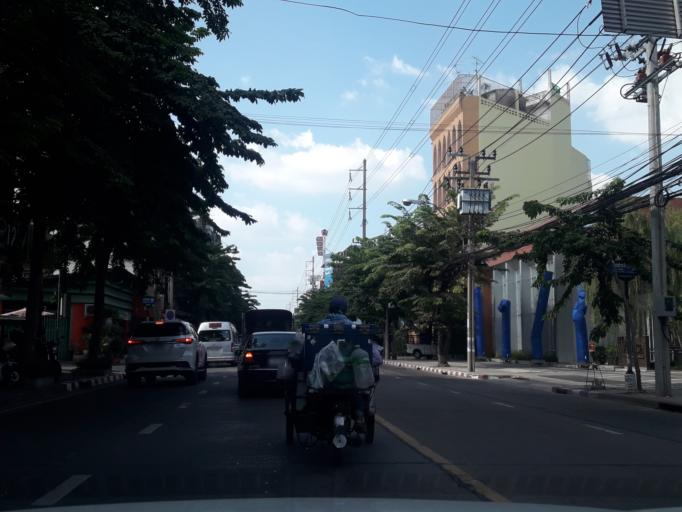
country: TH
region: Bangkok
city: Yan Nawa
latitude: 13.6962
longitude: 100.5326
